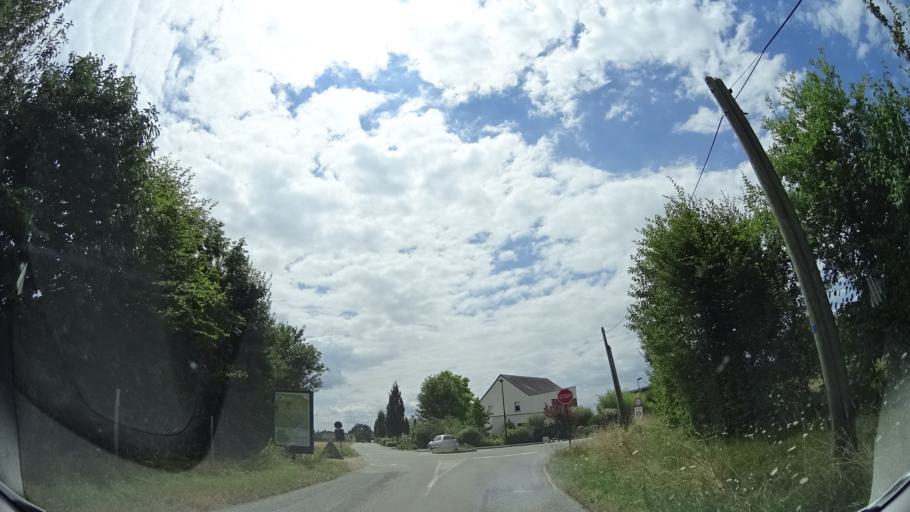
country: FR
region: Brittany
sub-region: Departement d'Ille-et-Vilaine
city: Pace
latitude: 48.1639
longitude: -1.7616
